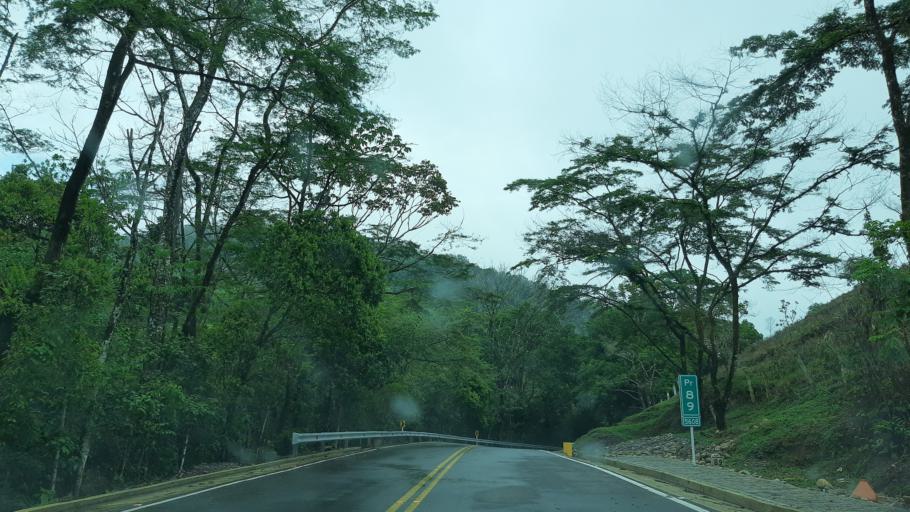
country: CO
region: Casanare
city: Sabanalarga
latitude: 4.7593
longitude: -73.0244
